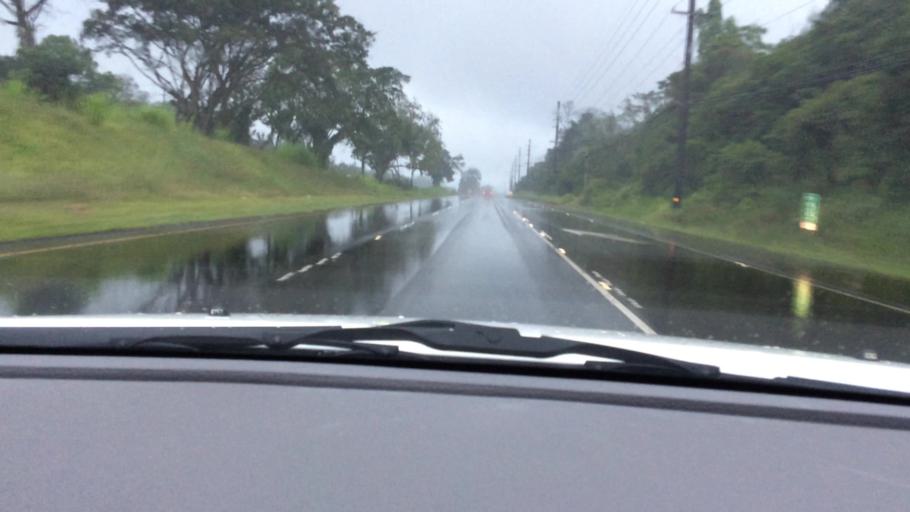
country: US
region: Hawaii
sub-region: Hawaii County
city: Kea'au
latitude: 19.6471
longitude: -155.0490
